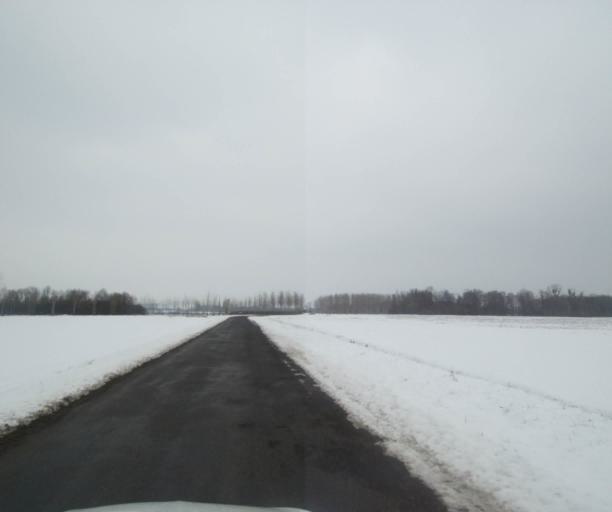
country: FR
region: Champagne-Ardenne
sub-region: Departement de la Haute-Marne
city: Saint-Dizier
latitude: 48.5685
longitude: 4.8910
